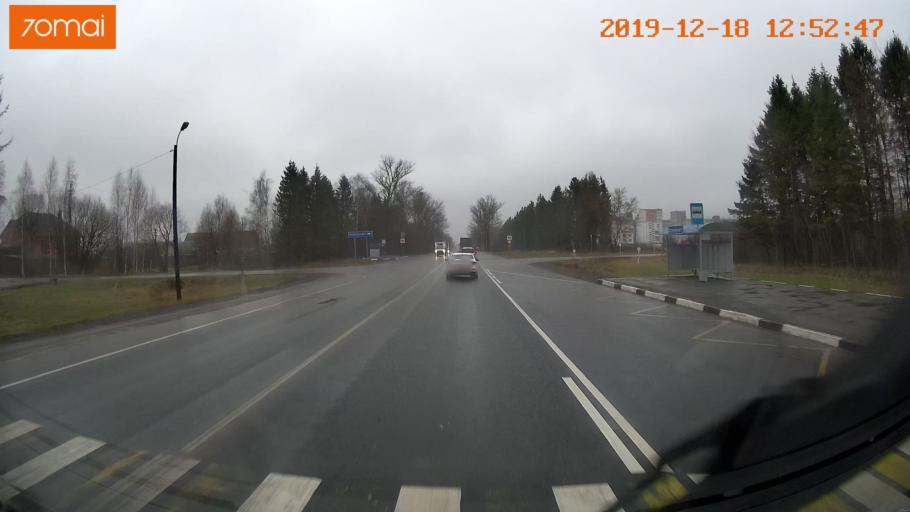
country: RU
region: Moskovskaya
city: Klin
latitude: 56.3139
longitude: 36.6898
